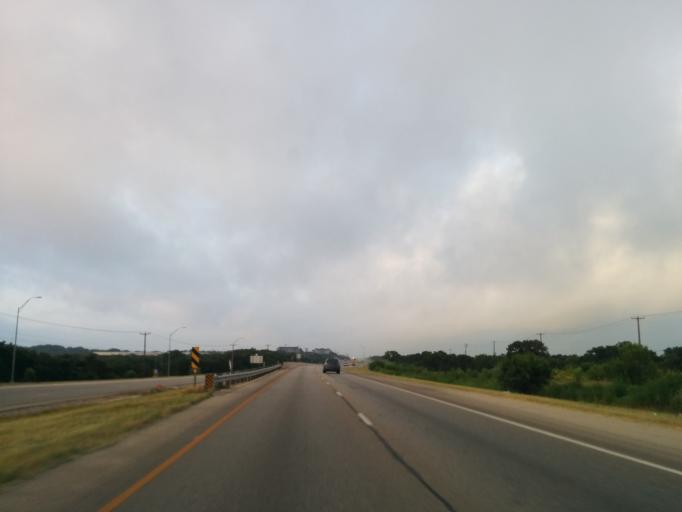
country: US
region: Texas
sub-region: Bexar County
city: Leon Valley
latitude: 29.4748
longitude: -98.7110
